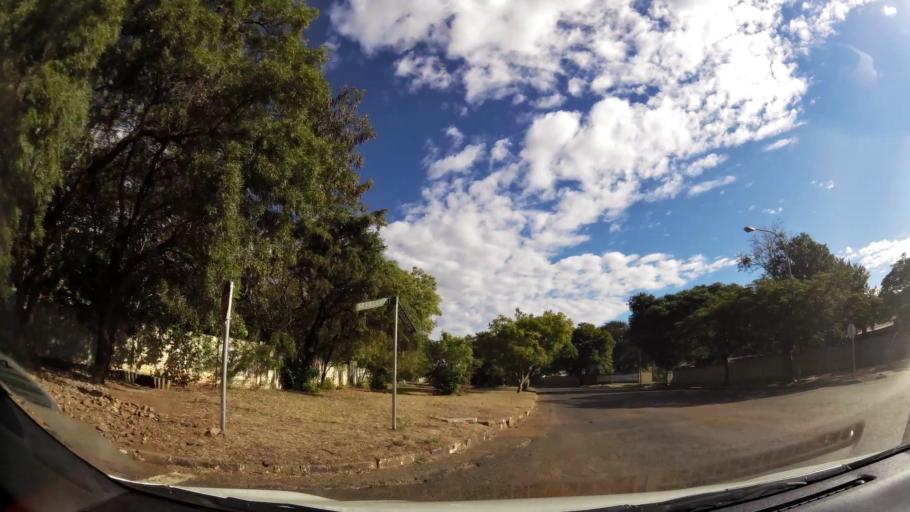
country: ZA
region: Limpopo
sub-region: Waterberg District Municipality
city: Warmbaths
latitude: -24.8832
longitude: 28.2803
